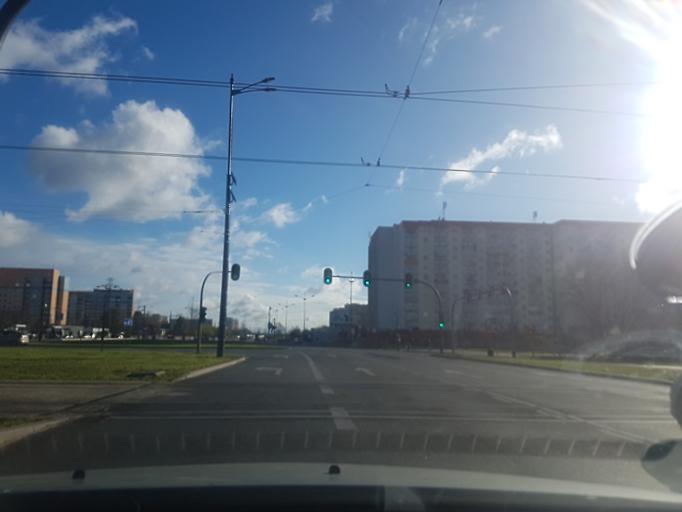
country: PL
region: Lodz Voivodeship
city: Lodz
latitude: 51.7605
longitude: 19.5366
